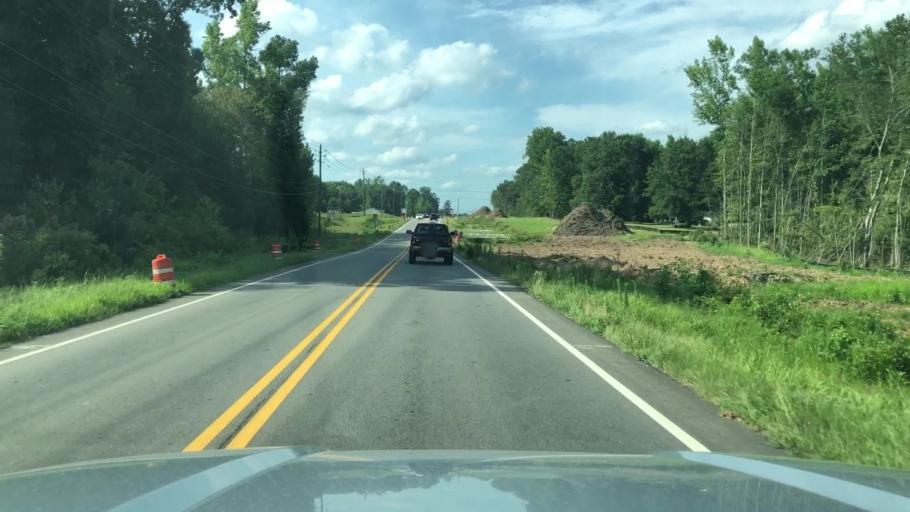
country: US
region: Georgia
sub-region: Paulding County
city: Hiram
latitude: 33.8294
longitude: -84.7592
